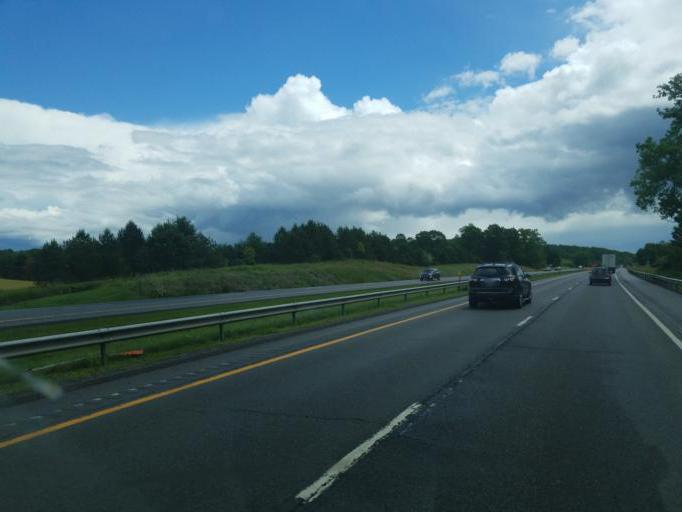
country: US
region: New York
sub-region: Ontario County
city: Victor
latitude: 43.0135
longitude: -77.4579
